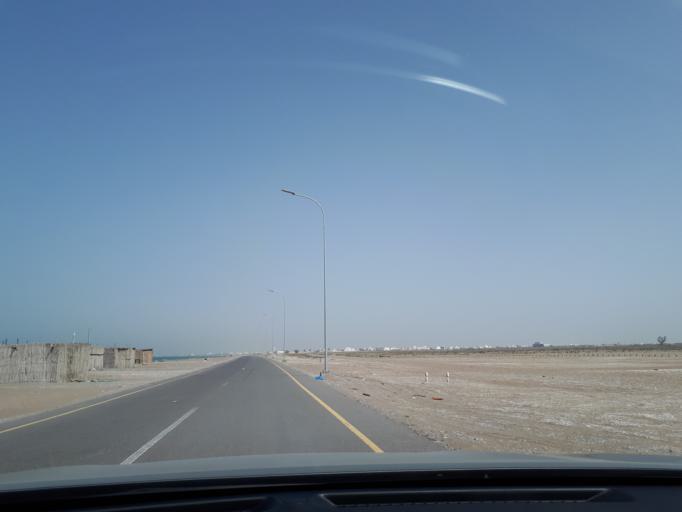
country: OM
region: Al Batinah
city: Barka'
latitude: 23.7280
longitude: 57.8410
